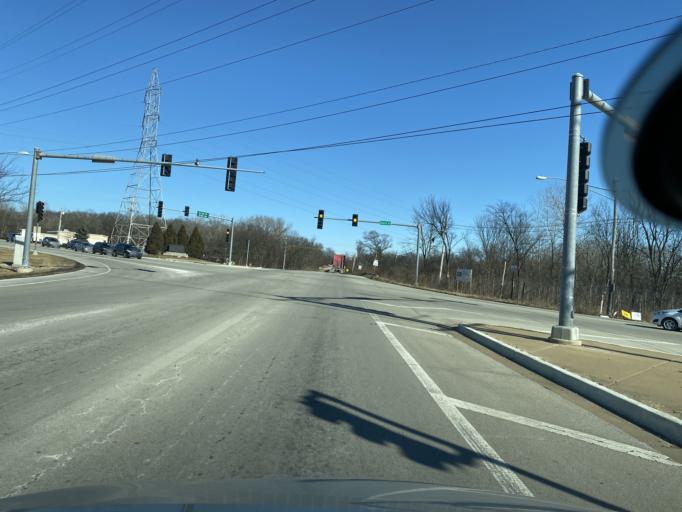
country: US
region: Illinois
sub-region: Cook County
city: Lemont
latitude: 41.6444
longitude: -87.9997
